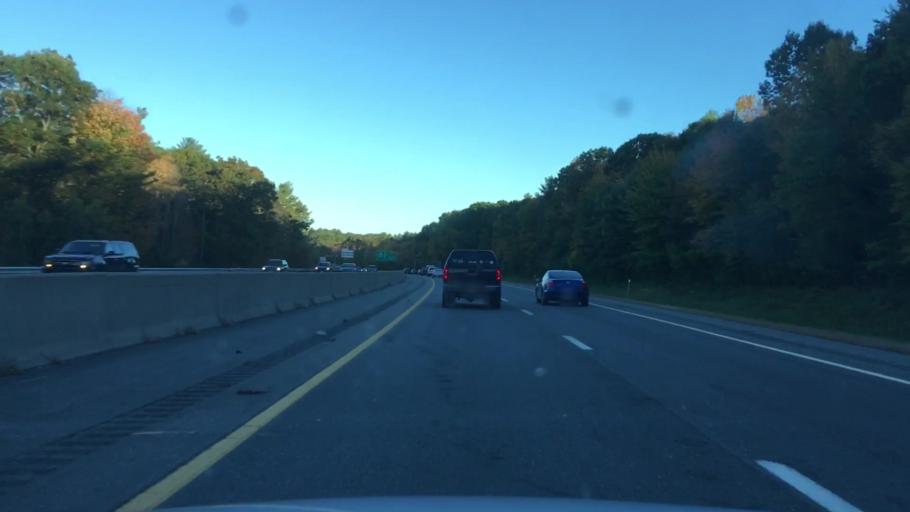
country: US
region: New Hampshire
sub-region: Rockingham County
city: Hampton
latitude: 42.9669
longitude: -70.8854
